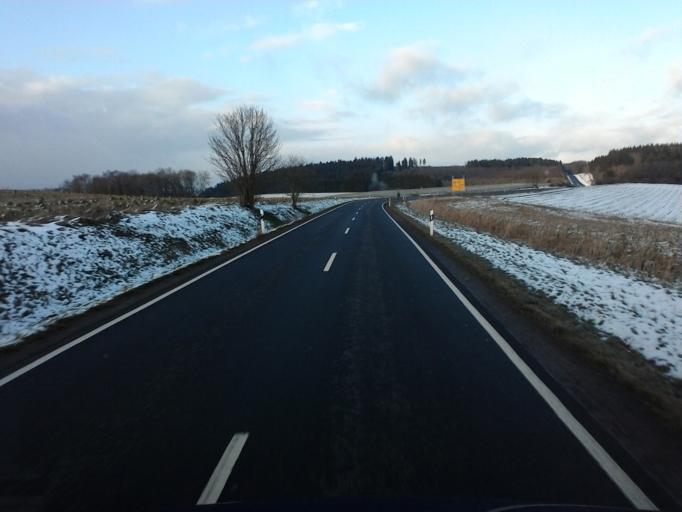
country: DE
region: Rheinland-Pfalz
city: Grosslangenfeld
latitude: 50.1984
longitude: 6.2465
